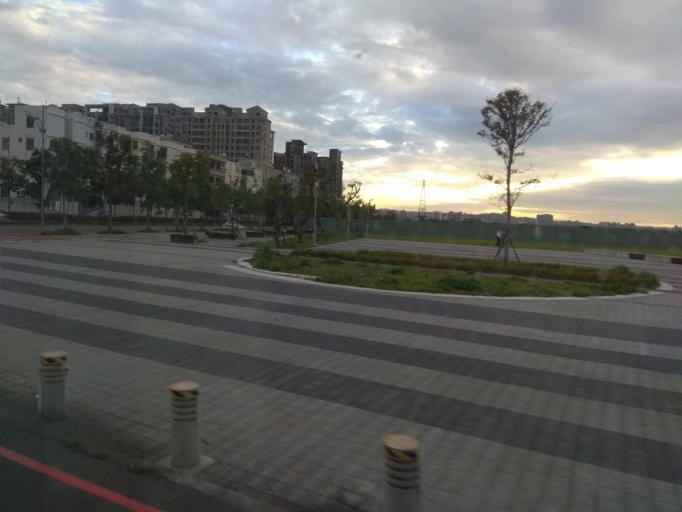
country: TW
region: Taiwan
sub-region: Hsinchu
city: Zhubei
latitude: 24.8246
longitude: 121.0079
